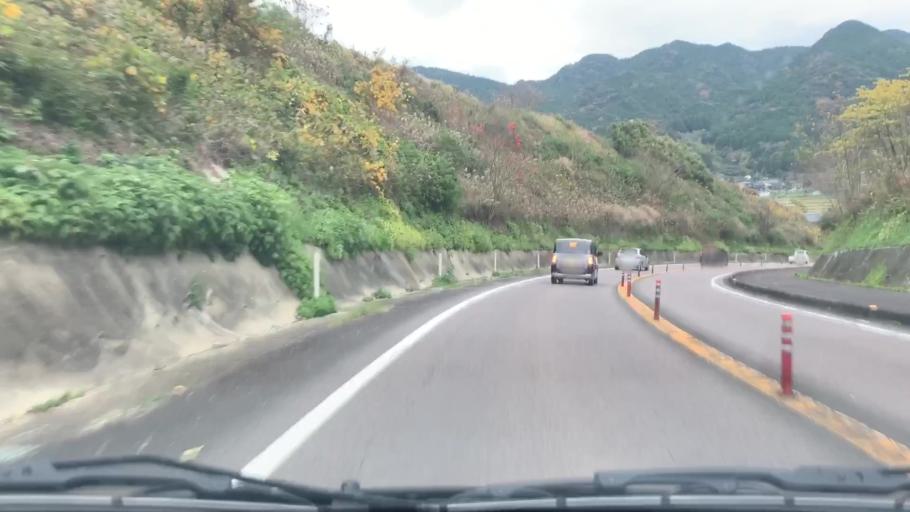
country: JP
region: Saga Prefecture
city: Ureshinomachi-shimojuku
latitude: 33.0883
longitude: 130.0175
